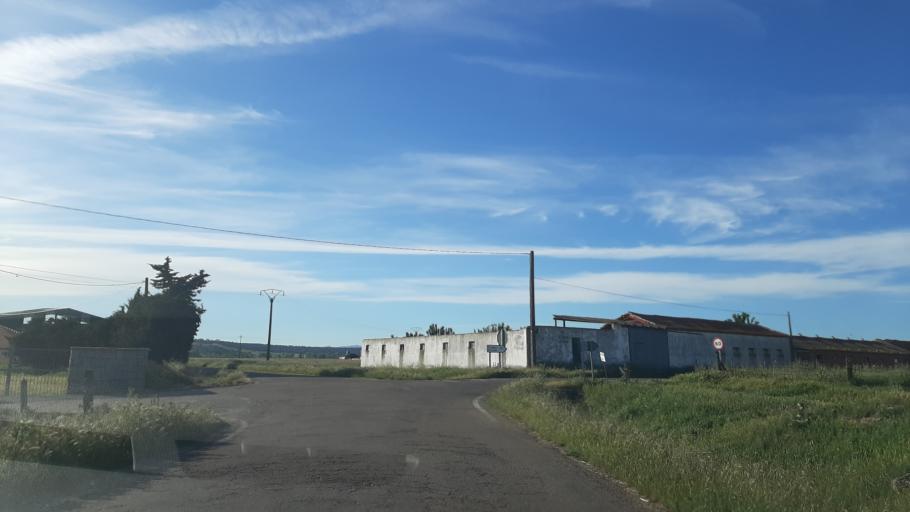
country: ES
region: Castille and Leon
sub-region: Provincia de Salamanca
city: Pedrosillo de Alba
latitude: 40.8208
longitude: -5.3964
